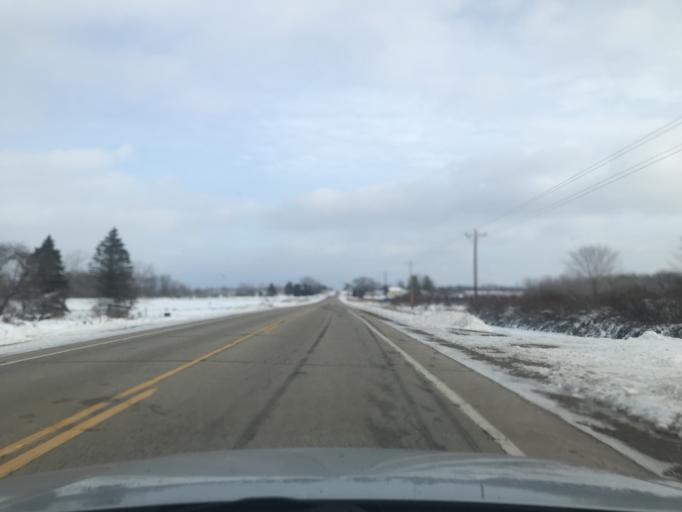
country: US
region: Wisconsin
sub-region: Oconto County
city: Oconto
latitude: 44.8932
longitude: -87.9848
